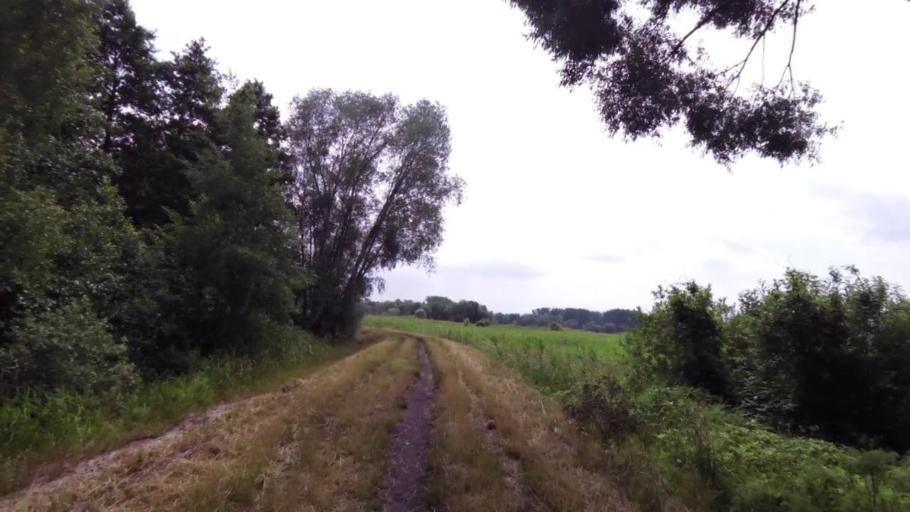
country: PL
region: West Pomeranian Voivodeship
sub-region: Szczecin
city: Szczecin
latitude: 53.4084
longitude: 14.6668
